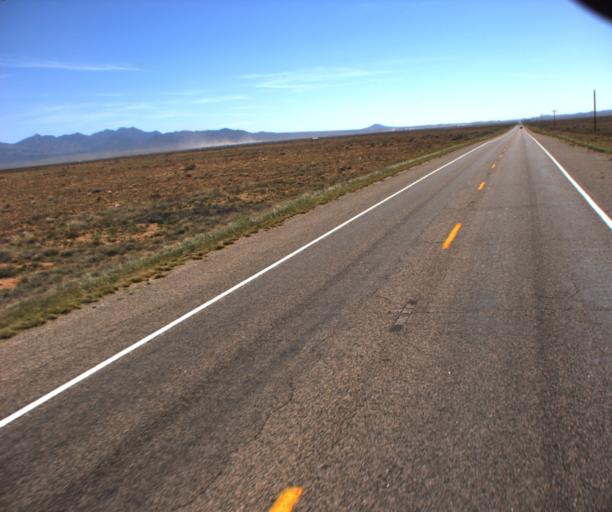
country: US
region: Arizona
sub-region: Mohave County
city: New Kingman-Butler
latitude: 35.3415
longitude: -113.8918
